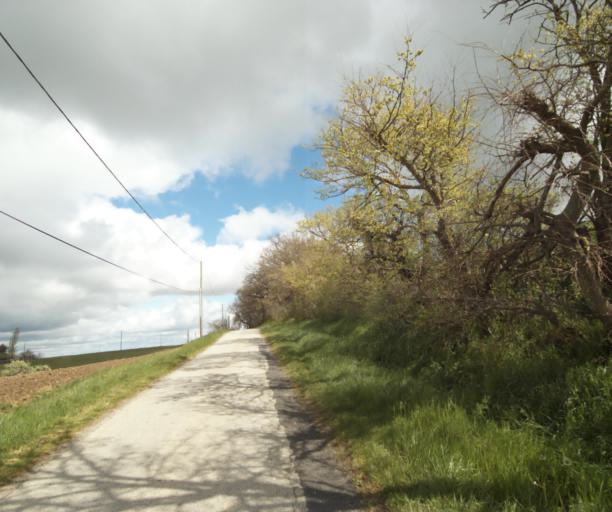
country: FR
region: Midi-Pyrenees
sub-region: Departement de l'Ariege
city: Saverdun
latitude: 43.1943
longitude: 1.5395
